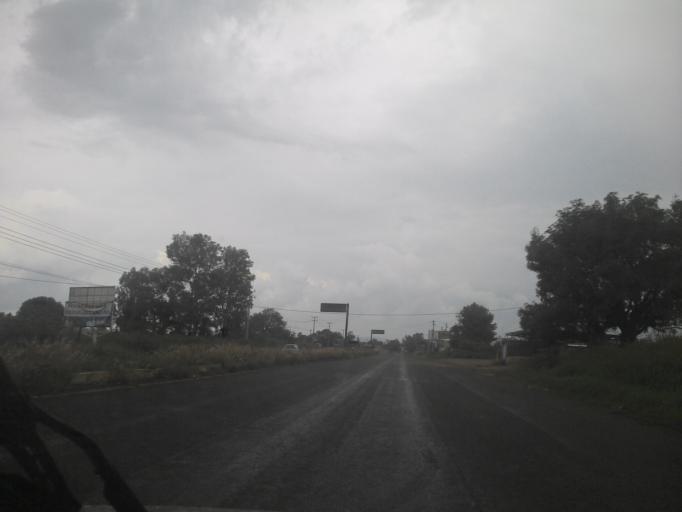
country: MX
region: Jalisco
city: Arandas
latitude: 20.7117
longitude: -102.4137
